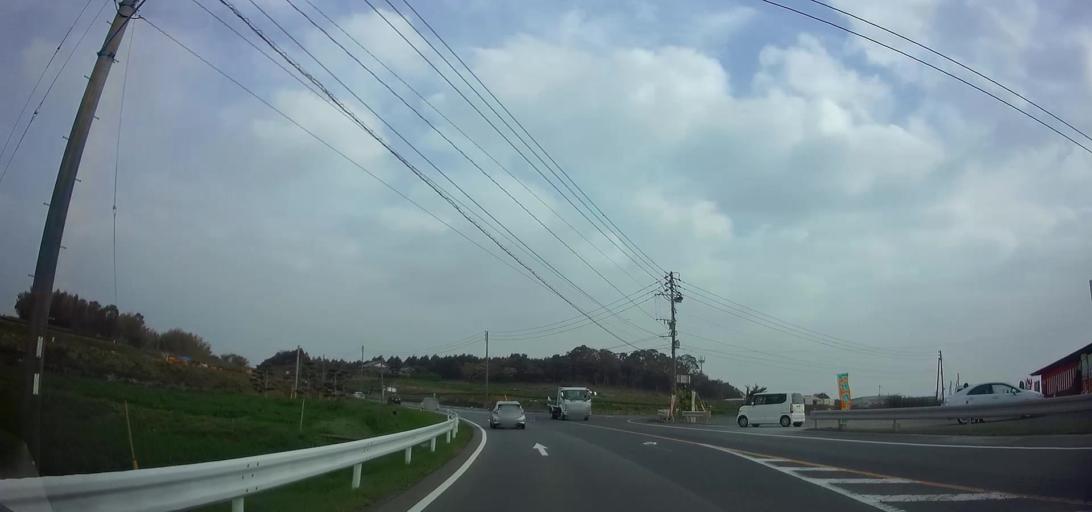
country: JP
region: Nagasaki
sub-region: Isahaya-shi
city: Isahaya
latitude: 32.7856
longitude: 130.0454
